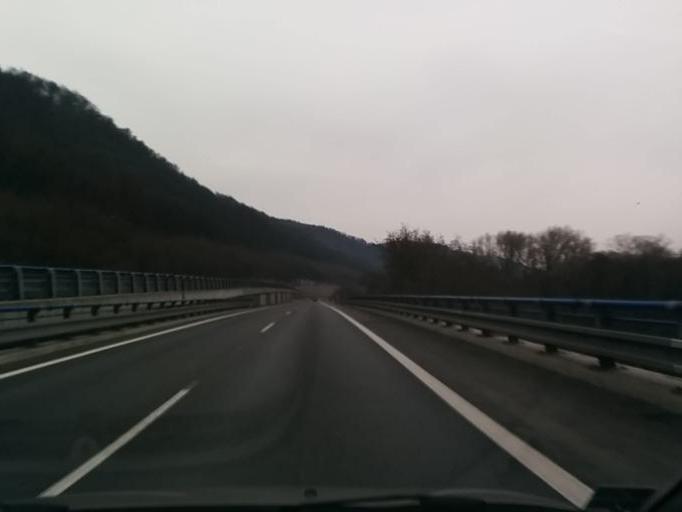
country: SK
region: Banskobystricky
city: Nova Bana
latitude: 48.4247
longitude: 18.6683
